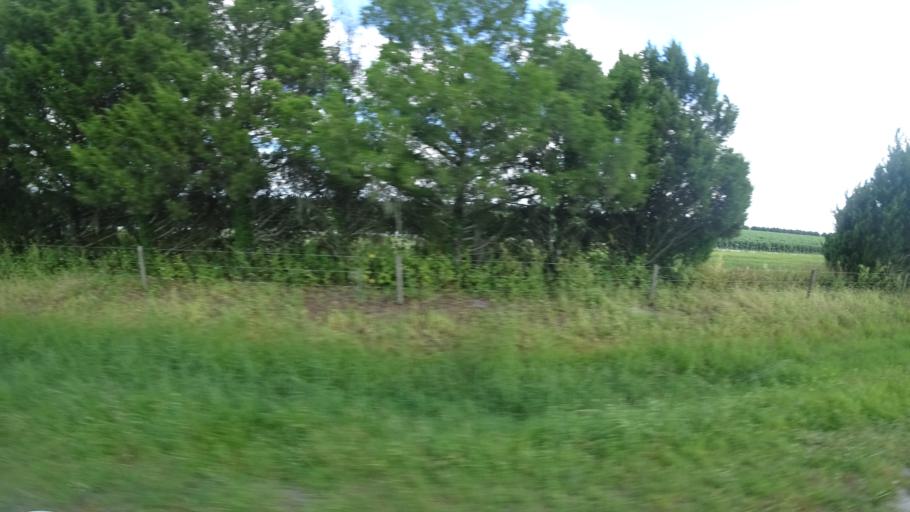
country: US
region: Florida
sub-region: DeSoto County
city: Arcadia
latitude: 27.3007
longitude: -82.1133
